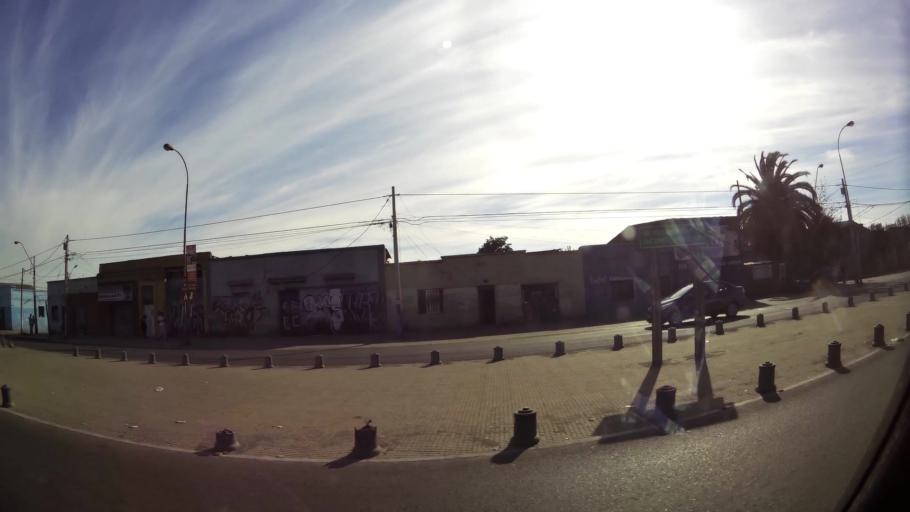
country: CL
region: Santiago Metropolitan
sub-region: Provincia de Santiago
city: Santiago
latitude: -33.4630
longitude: -70.6882
